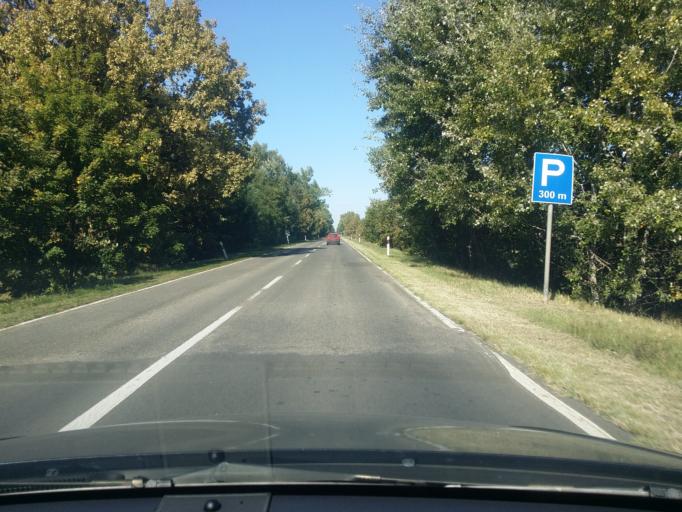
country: HU
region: Csongrad
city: Pusztaszer
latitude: 46.5403
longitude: 19.9563
